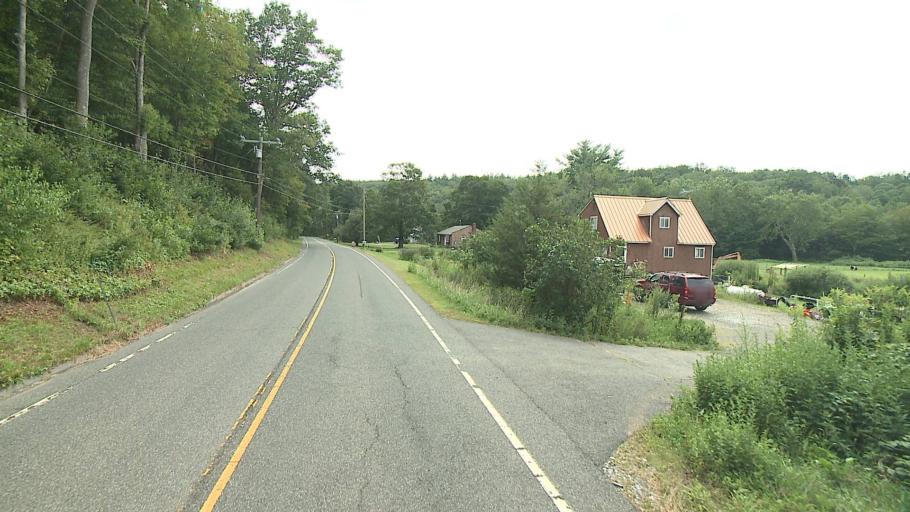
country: US
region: Connecticut
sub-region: Litchfield County
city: Woodbury
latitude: 41.5800
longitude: -73.2296
